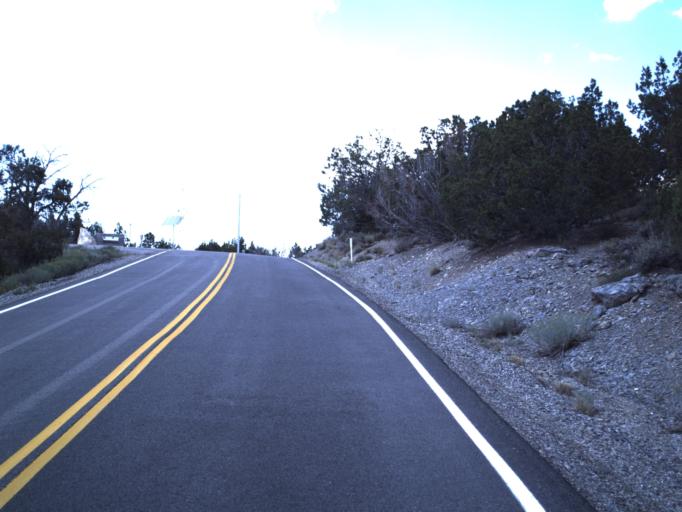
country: US
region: Utah
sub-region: Tooele County
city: Grantsville
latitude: 40.3369
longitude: -112.5720
